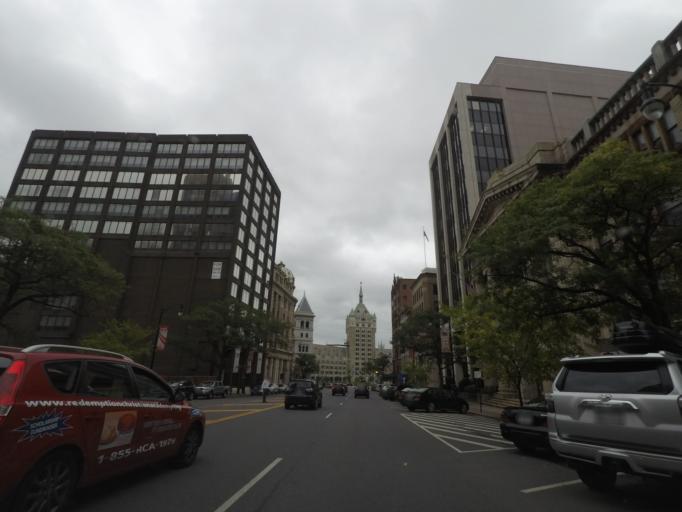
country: US
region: New York
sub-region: Albany County
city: Albany
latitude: 42.6494
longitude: -73.7522
